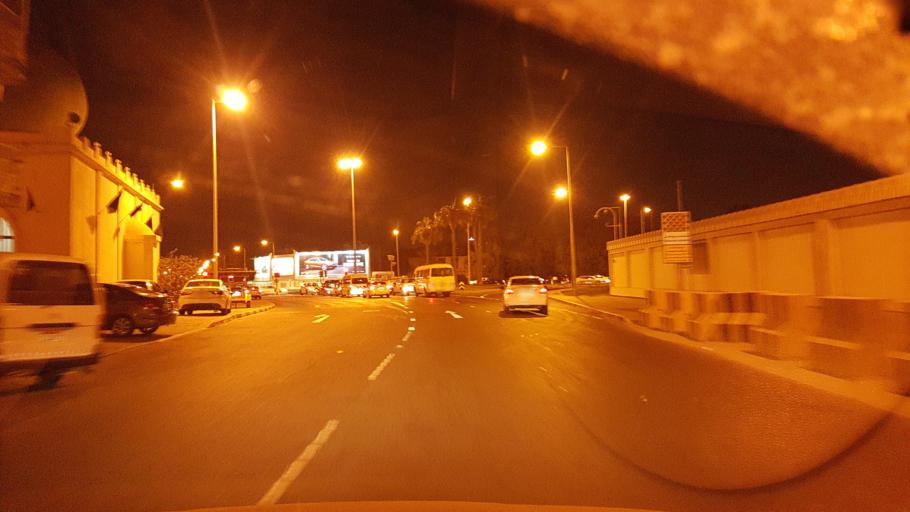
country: BH
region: Manama
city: Manama
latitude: 26.2203
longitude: 50.5782
